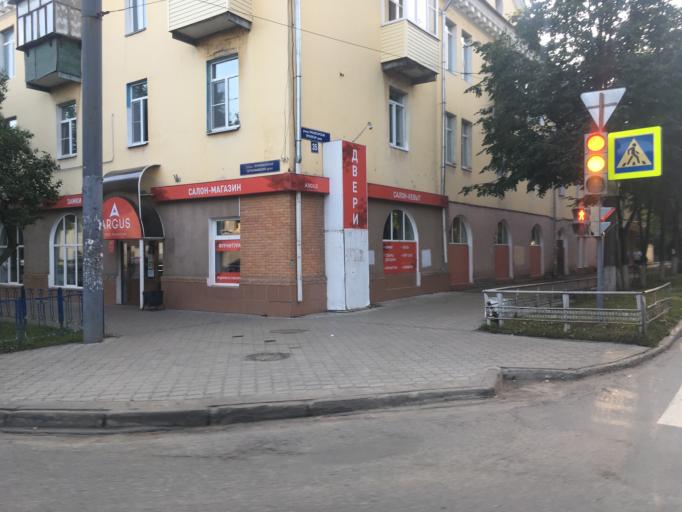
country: RU
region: Mariy-El
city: Yoshkar-Ola
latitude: 56.6457
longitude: 47.8919
